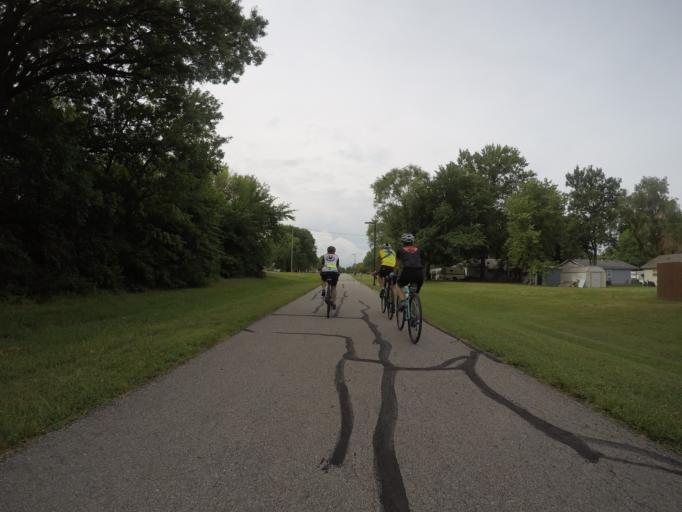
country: US
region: Kansas
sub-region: Franklin County
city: Ottawa
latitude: 38.6056
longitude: -95.2701
